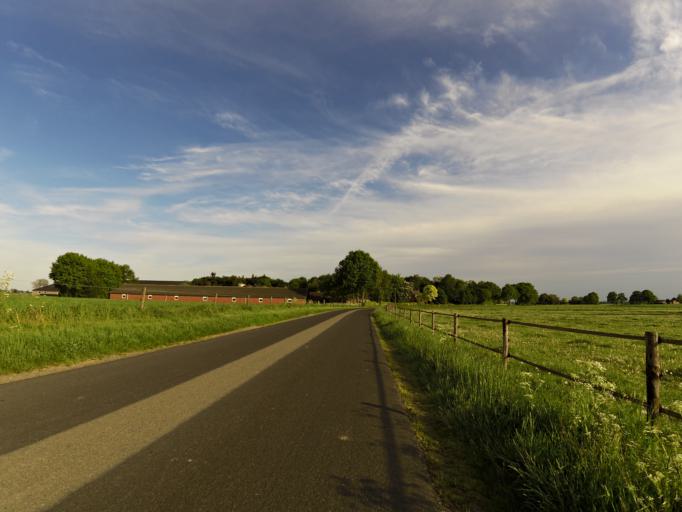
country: NL
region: Gelderland
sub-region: Gemeente Doetinchem
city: Doetinchem
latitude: 51.9293
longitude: 6.2833
